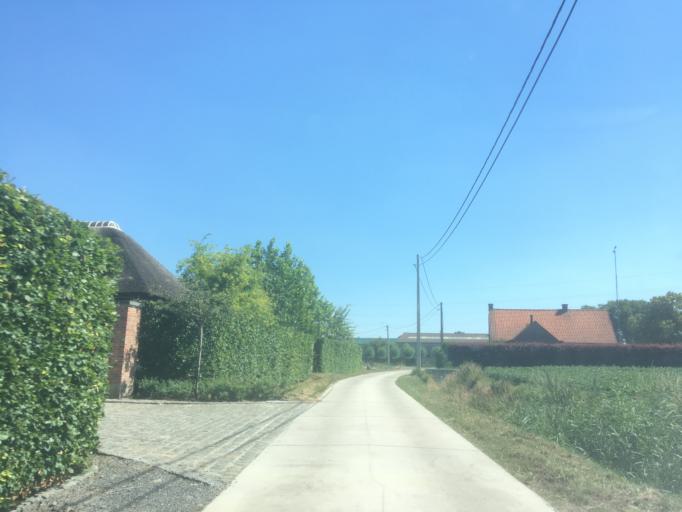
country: BE
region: Flanders
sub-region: Provincie West-Vlaanderen
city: Ardooie
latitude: 50.9639
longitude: 3.1851
